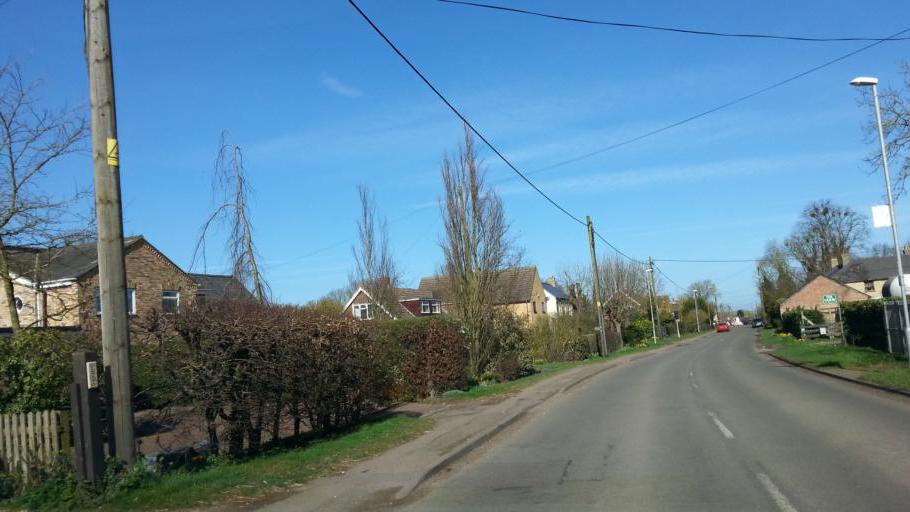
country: GB
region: England
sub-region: Cambridgeshire
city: Swavesey
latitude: 52.2857
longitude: -0.0050
